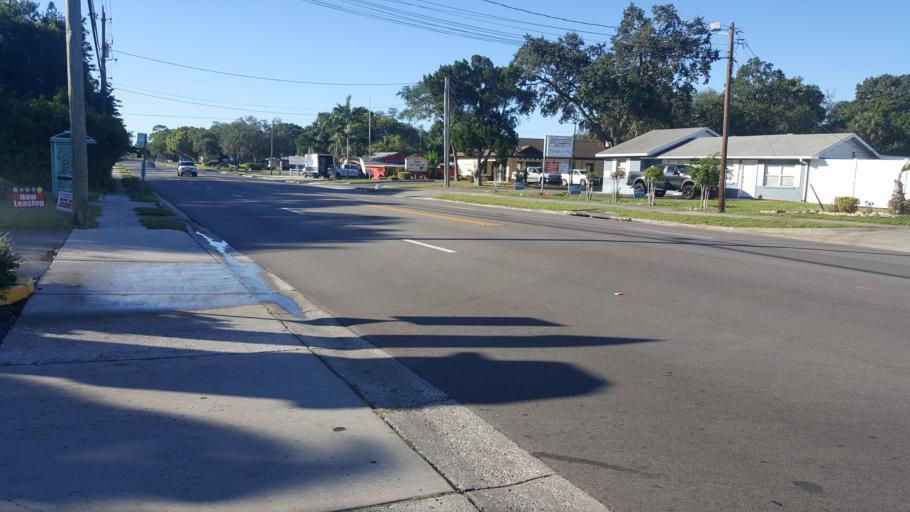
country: US
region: Florida
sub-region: Manatee County
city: South Bradenton
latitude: 27.4589
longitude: -82.5875
